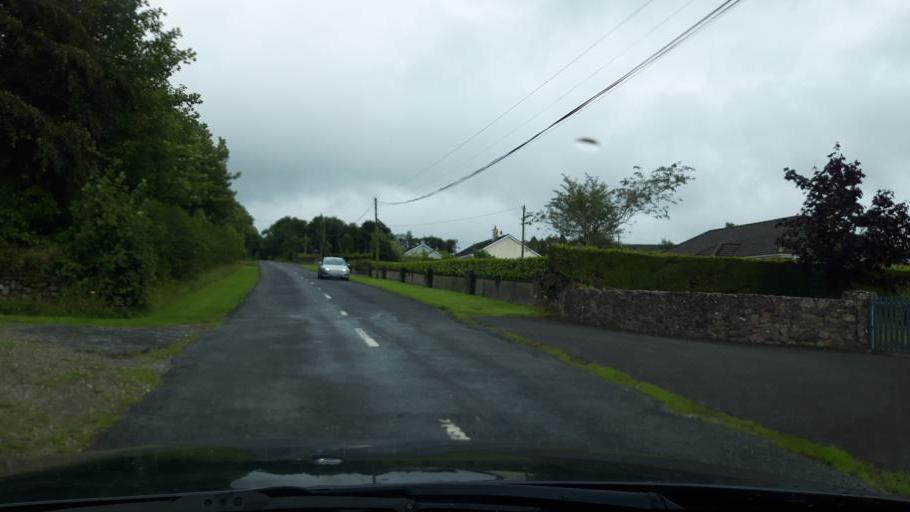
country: IE
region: Munster
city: Cahir
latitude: 52.1768
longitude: -7.8503
